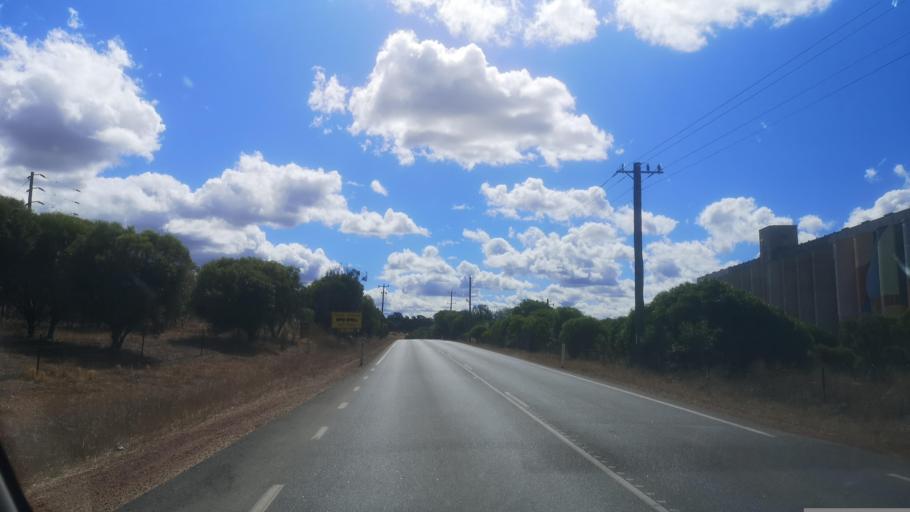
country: AU
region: Western Australia
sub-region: Northam
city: Northam
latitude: -31.6427
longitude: 116.6307
